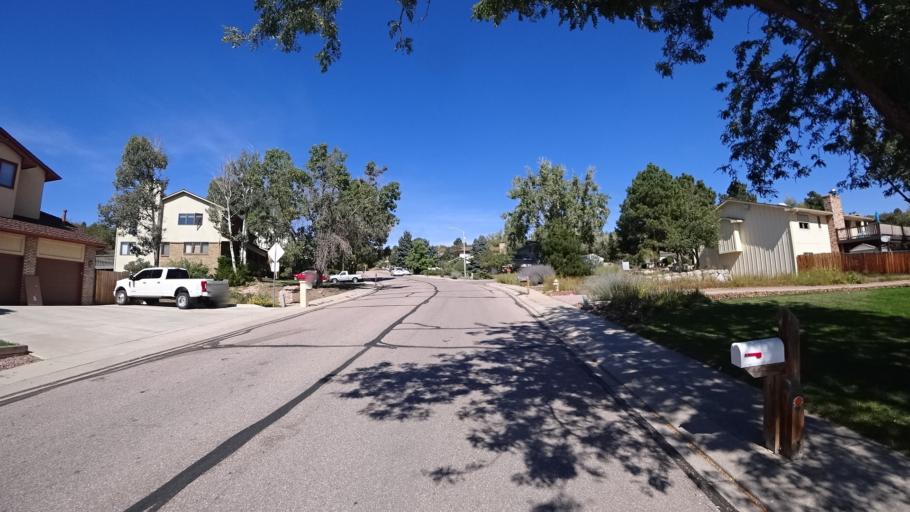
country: US
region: Colorado
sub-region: El Paso County
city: Cimarron Hills
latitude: 38.9122
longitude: -104.7580
